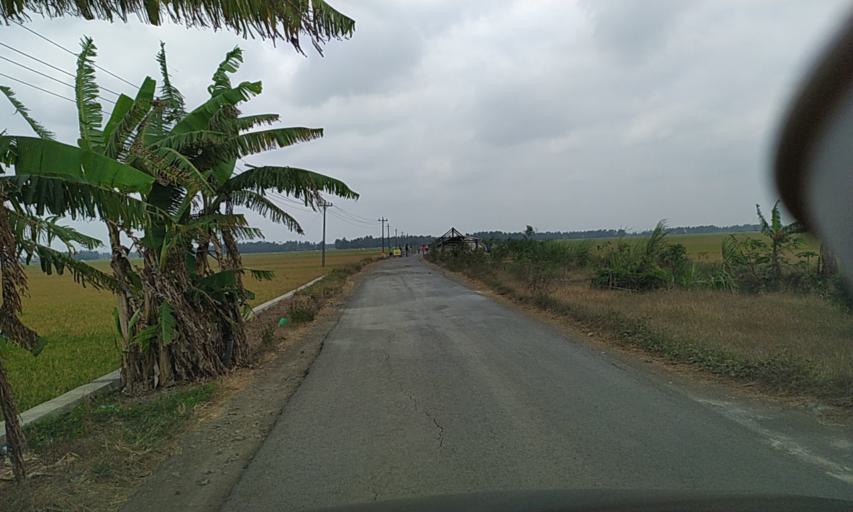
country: ID
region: Central Java
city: Sidakaya
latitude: -7.6172
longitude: 108.9269
